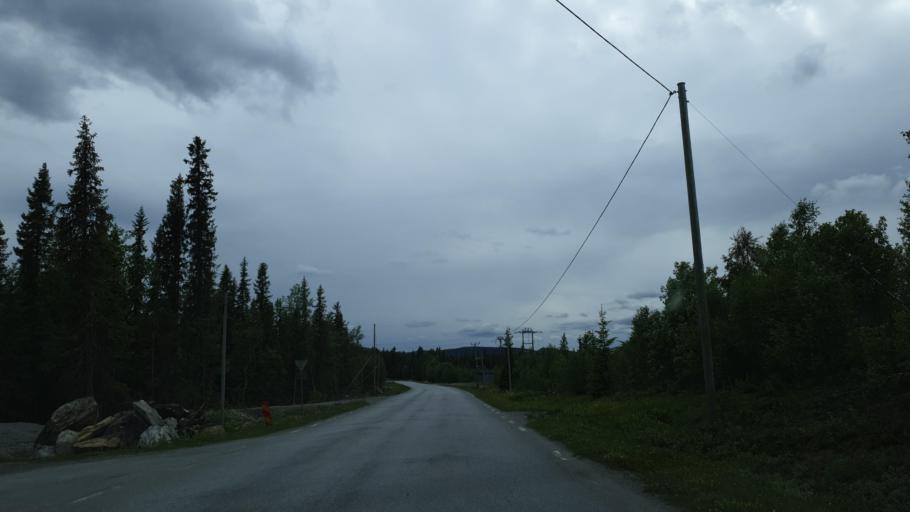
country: SE
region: Vaesterbotten
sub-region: Storumans Kommun
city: Fristad
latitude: 65.4281
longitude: 16.1752
